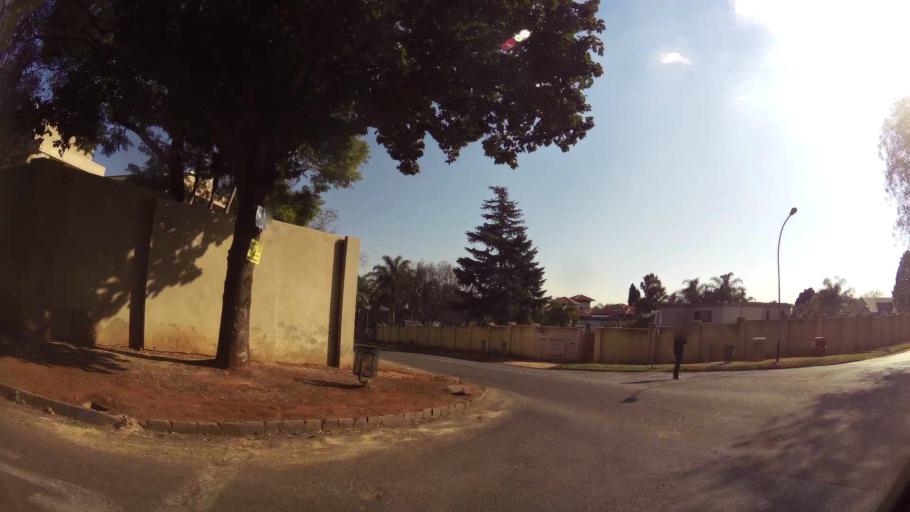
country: ZA
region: Gauteng
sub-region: Ekurhuleni Metropolitan Municipality
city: Germiston
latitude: -26.1802
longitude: 28.1451
